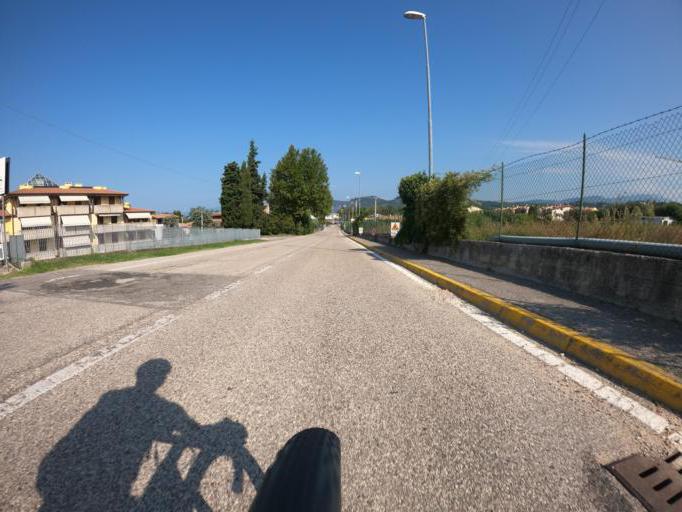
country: IT
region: Veneto
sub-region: Provincia di Verona
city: Bardolino
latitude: 45.5452
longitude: 10.7293
